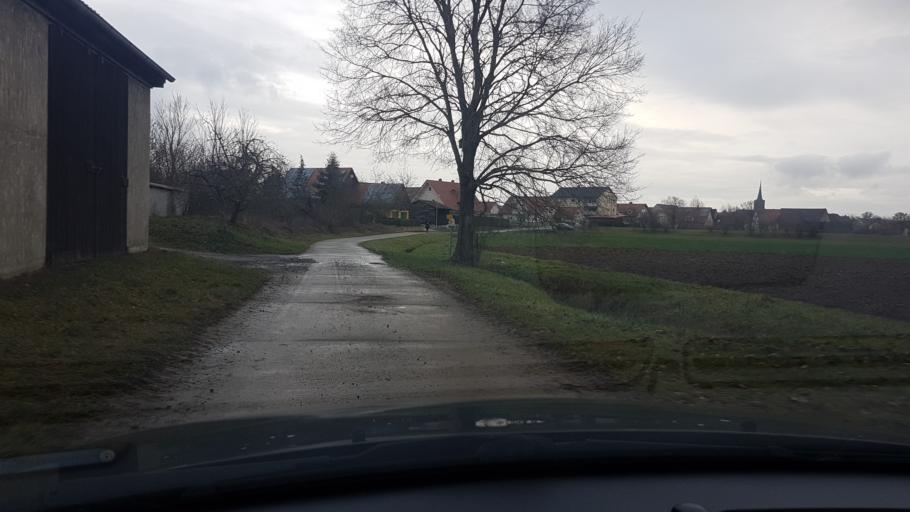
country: DE
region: Bavaria
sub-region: Upper Franconia
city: Rattelsdorf
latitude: 50.0044
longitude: 10.9004
